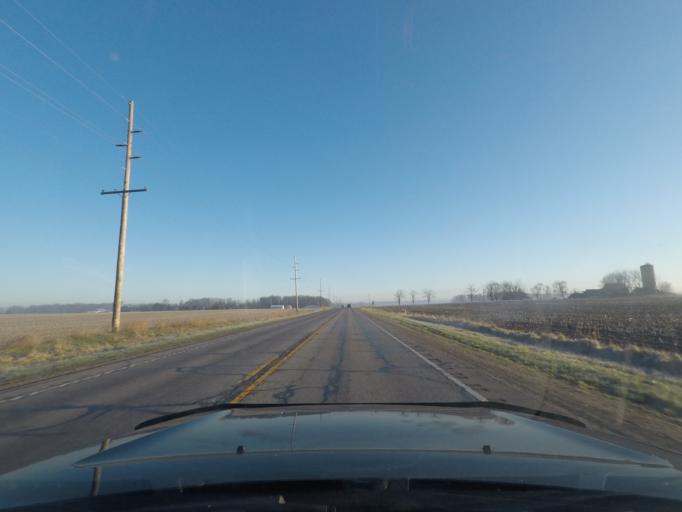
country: US
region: Indiana
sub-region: Elkhart County
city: Wakarusa
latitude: 41.5024
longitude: -86.0020
